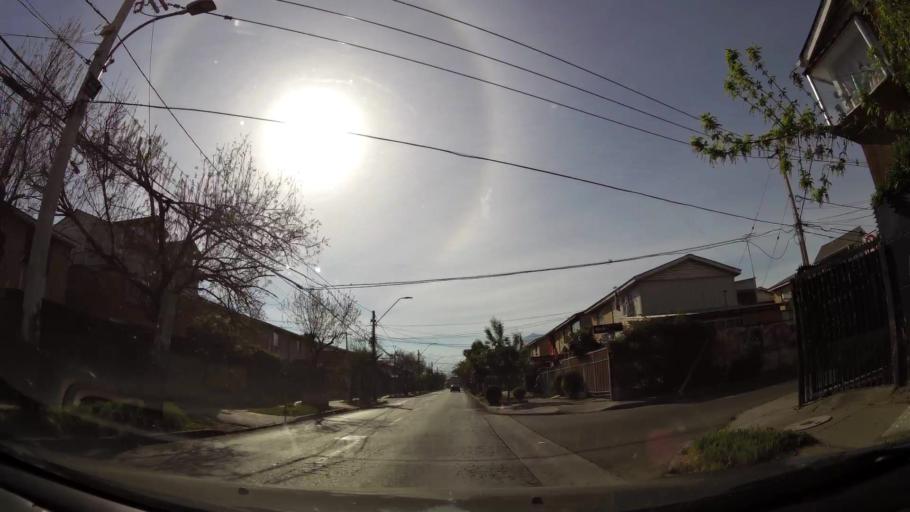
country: CL
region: Santiago Metropolitan
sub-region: Provincia de Cordillera
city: Puente Alto
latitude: -33.6105
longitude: -70.5958
